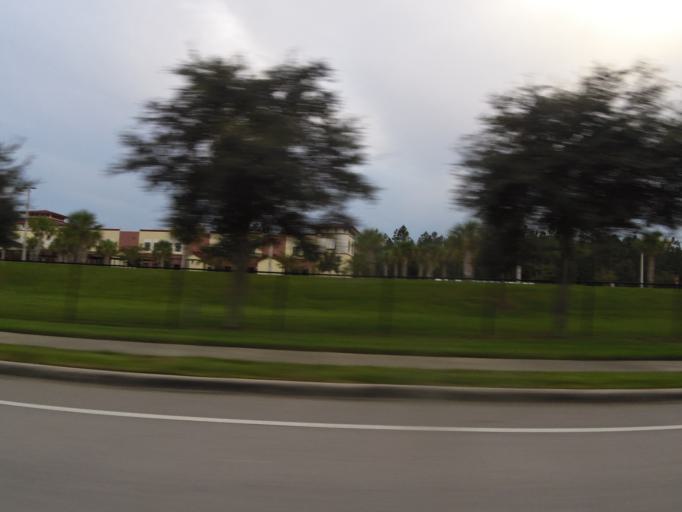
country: US
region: Florida
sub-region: Saint Johns County
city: Fruit Cove
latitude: 30.0841
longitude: -81.5390
